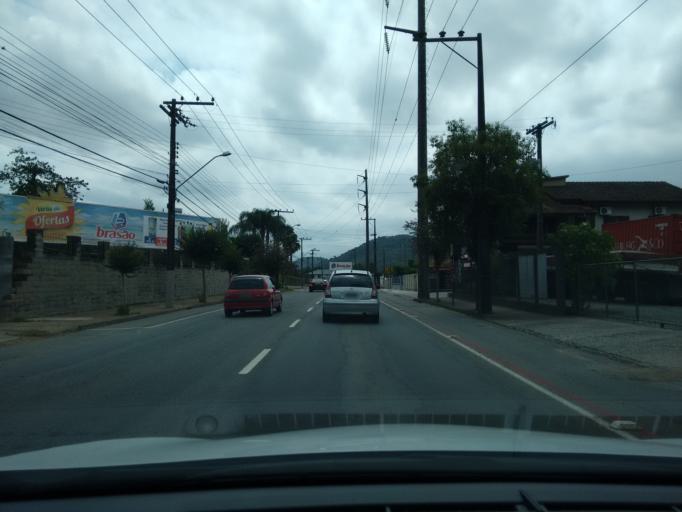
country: BR
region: Santa Catarina
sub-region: Jaragua Do Sul
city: Jaragua do Sul
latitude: -26.5100
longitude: -49.1100
